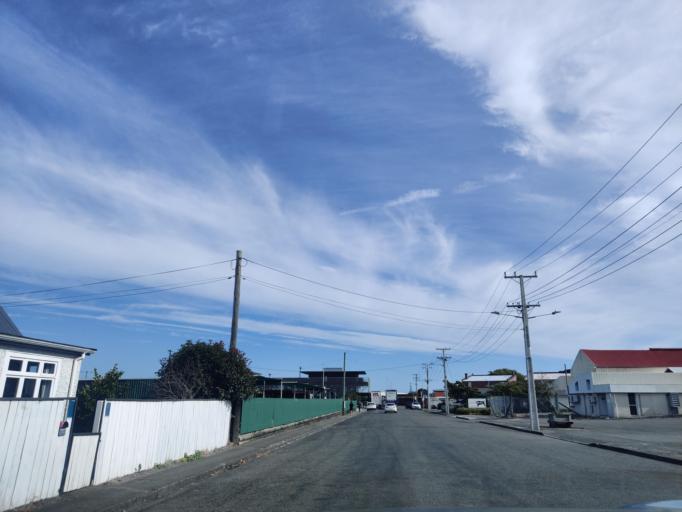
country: NZ
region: Manawatu-Wanganui
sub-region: Rangitikei District
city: Bulls
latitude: -40.1744
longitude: 175.3869
